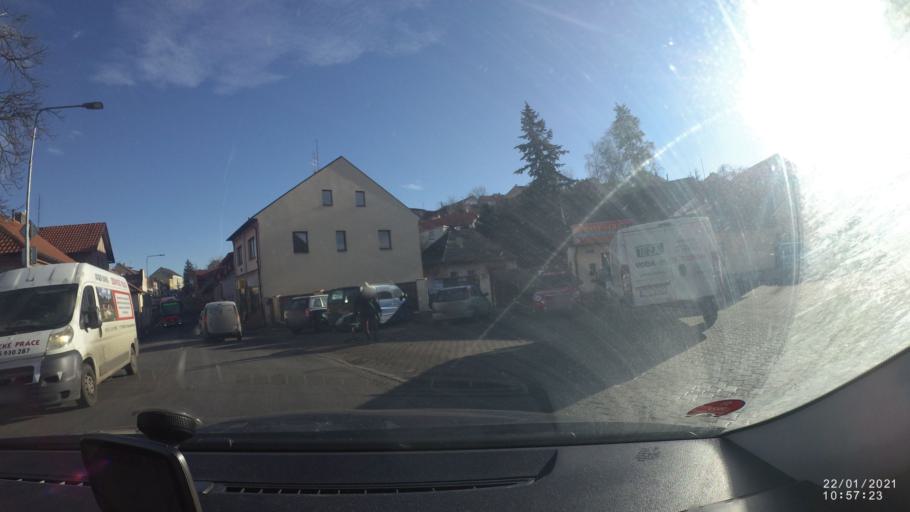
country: CZ
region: Central Bohemia
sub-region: Okres Beroun
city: Horovice
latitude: 49.8375
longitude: 13.8980
